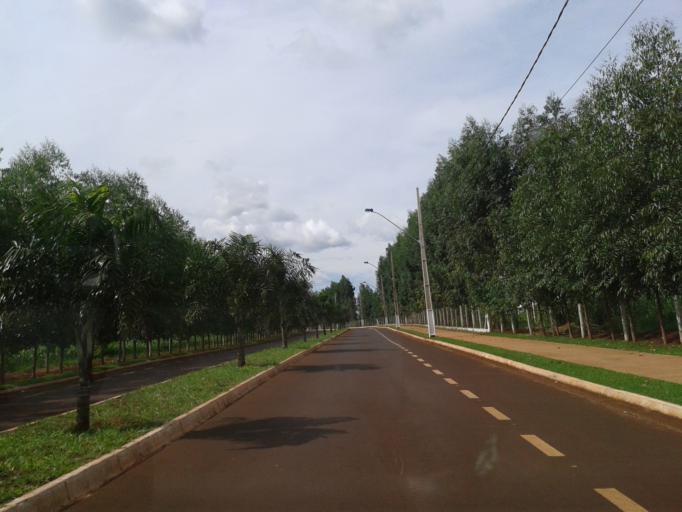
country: BR
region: Minas Gerais
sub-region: Centralina
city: Centralina
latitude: -18.5752
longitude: -49.1963
